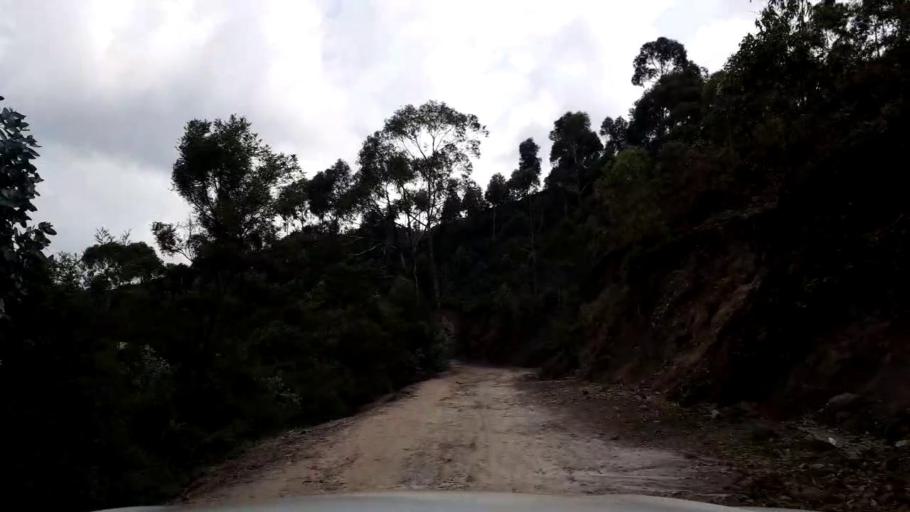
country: RW
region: Western Province
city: Kibuye
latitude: -1.9606
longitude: 29.4772
